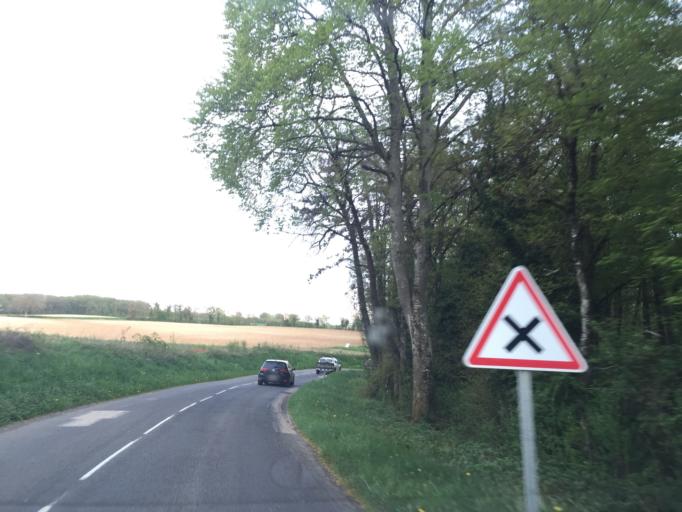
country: FR
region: Rhone-Alpes
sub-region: Departement de l'Isere
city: Salagnon
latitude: 45.7387
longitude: 5.3665
